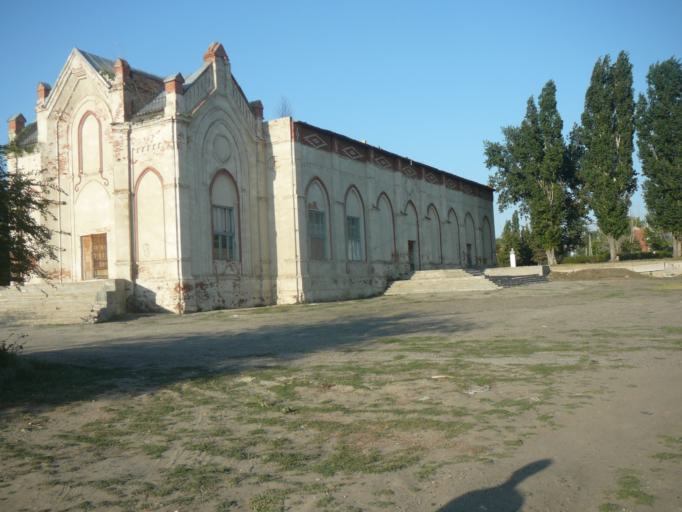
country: RU
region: Saratov
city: Sovetskoye
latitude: 51.5101
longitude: 46.6293
